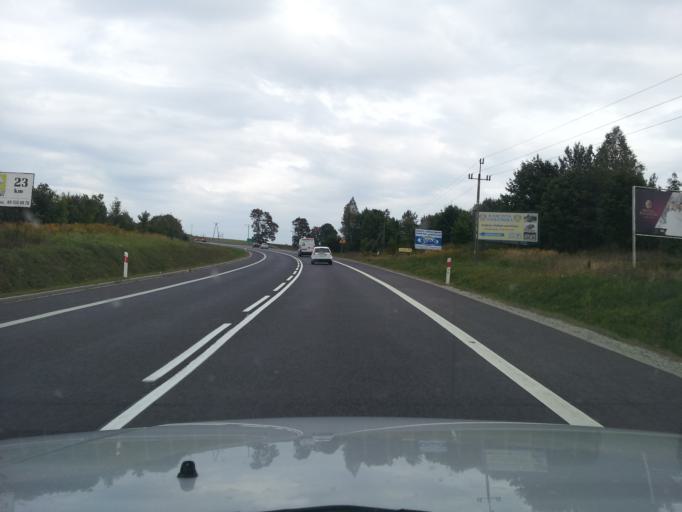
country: PL
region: Warmian-Masurian Voivodeship
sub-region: Powiat olsztynski
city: Gietrzwald
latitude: 53.7443
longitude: 20.2345
